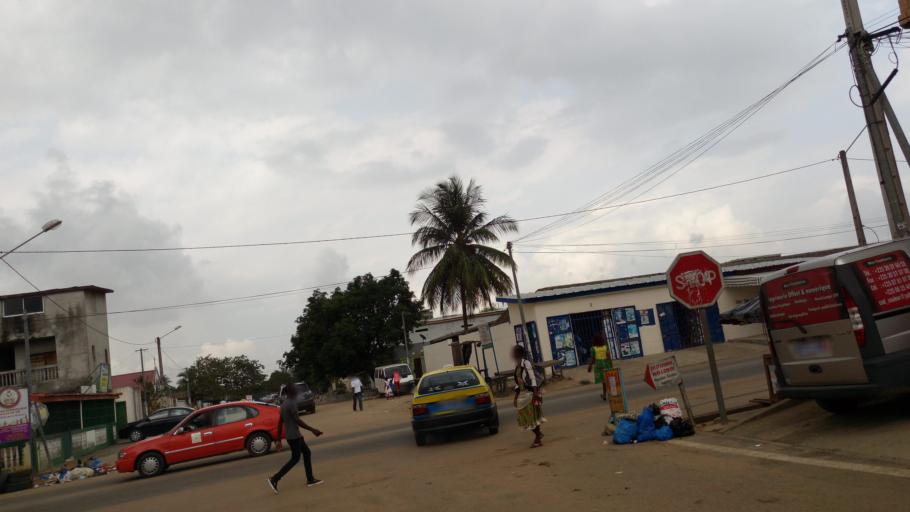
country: CI
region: Lagunes
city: Abobo
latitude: 5.4002
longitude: -4.0044
